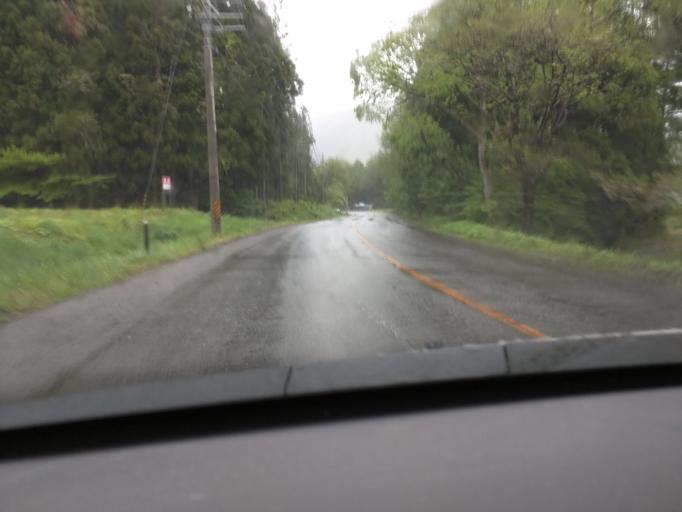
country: JP
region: Fukushima
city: Inawashiro
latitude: 37.6011
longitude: 140.1249
